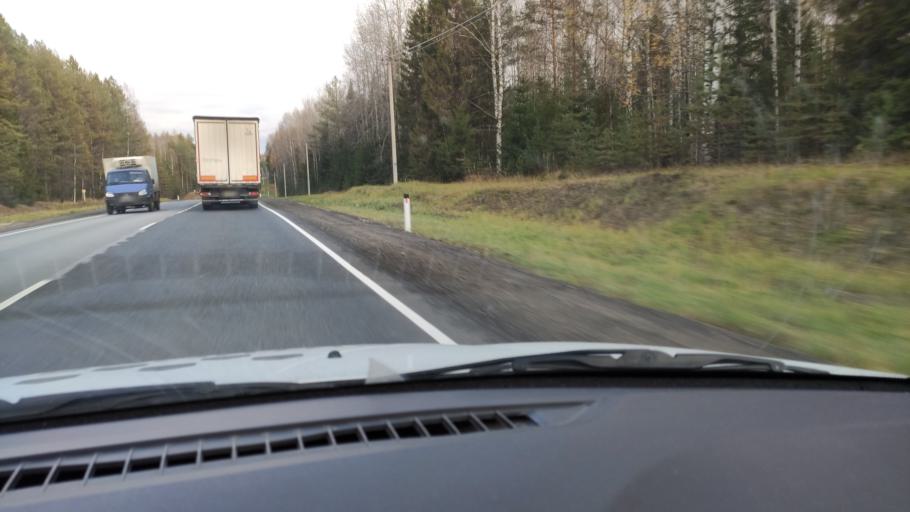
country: RU
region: Kirov
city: Dubrovka
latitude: 58.9139
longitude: 51.1606
